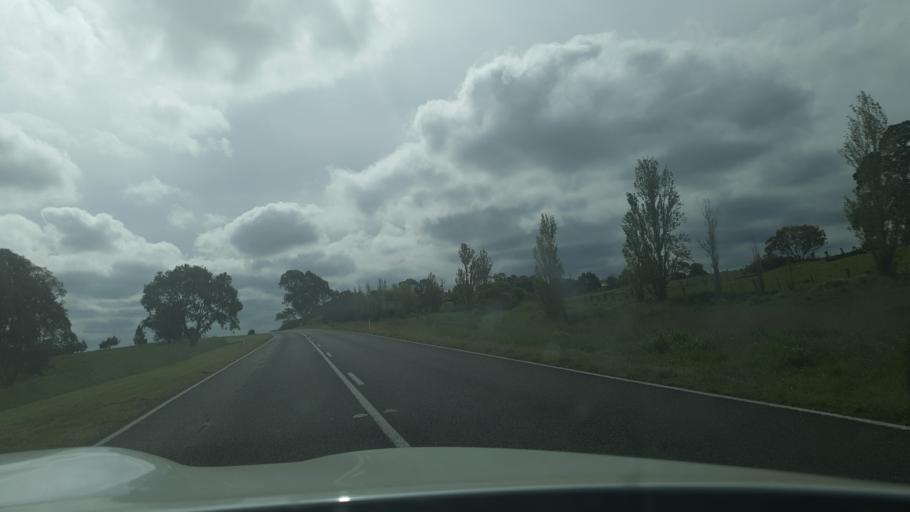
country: AU
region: Victoria
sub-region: Central Goldfields
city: Maryborough
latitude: -37.2089
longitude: 143.7197
